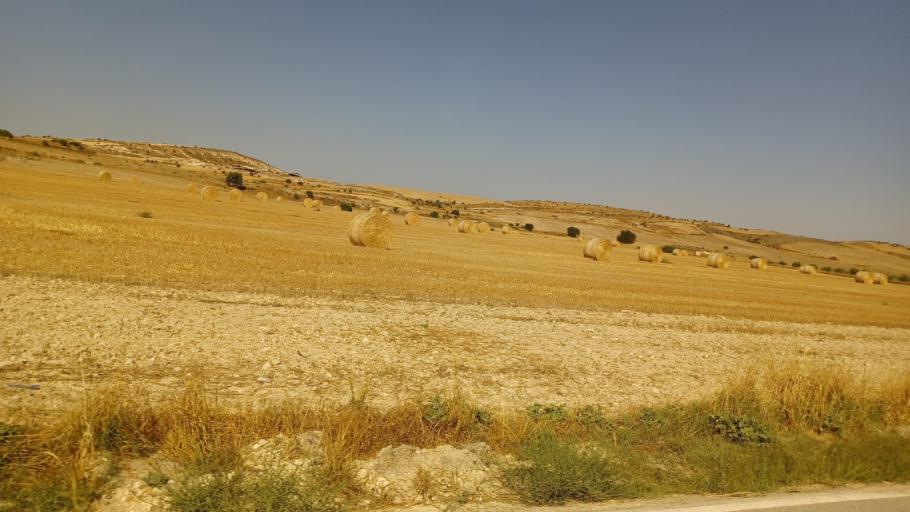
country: CY
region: Larnaka
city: Athienou
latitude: 35.0306
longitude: 33.5132
